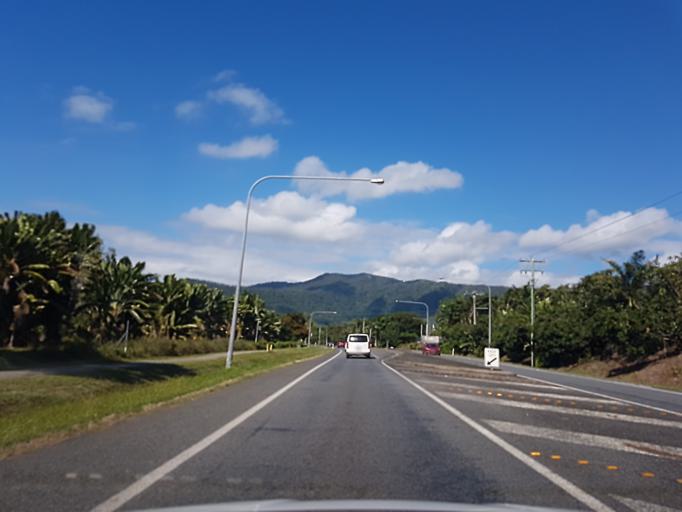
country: AU
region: Queensland
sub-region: Cairns
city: Trinity Beach
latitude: -16.7813
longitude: 145.6738
